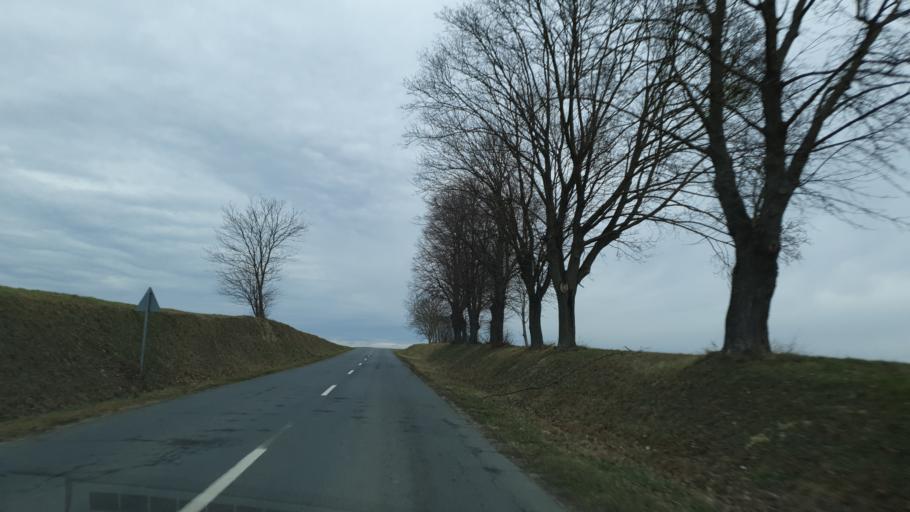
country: HU
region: Zala
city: Sarmellek
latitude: 46.6779
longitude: 17.1092
